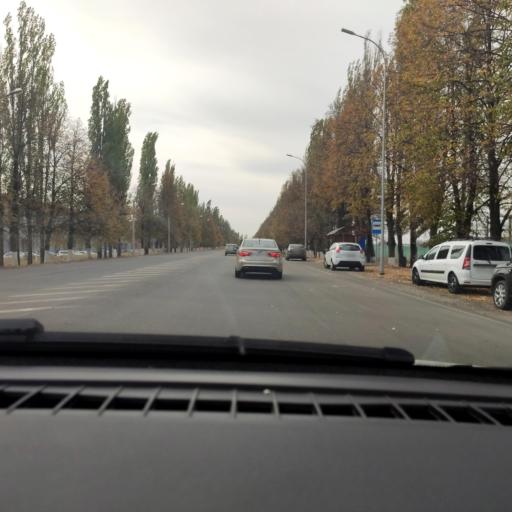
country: RU
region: Voronezj
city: Podgornoye
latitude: 51.8076
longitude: 39.2183
